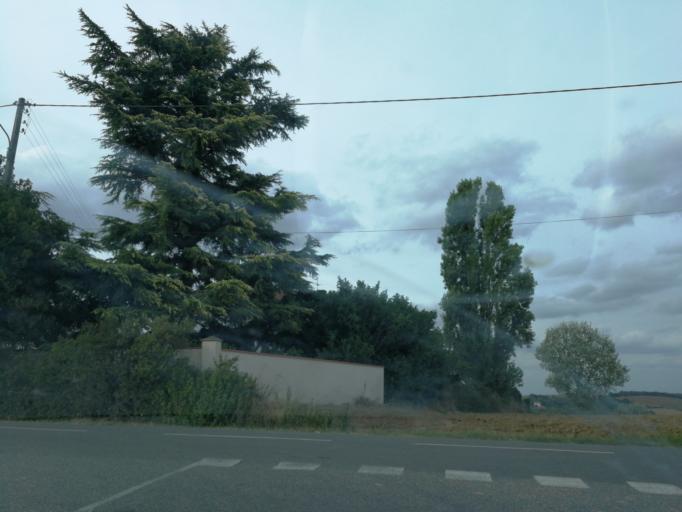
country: FR
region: Midi-Pyrenees
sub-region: Departement de la Haute-Garonne
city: Flourens
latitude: 43.6095
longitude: 1.5372
